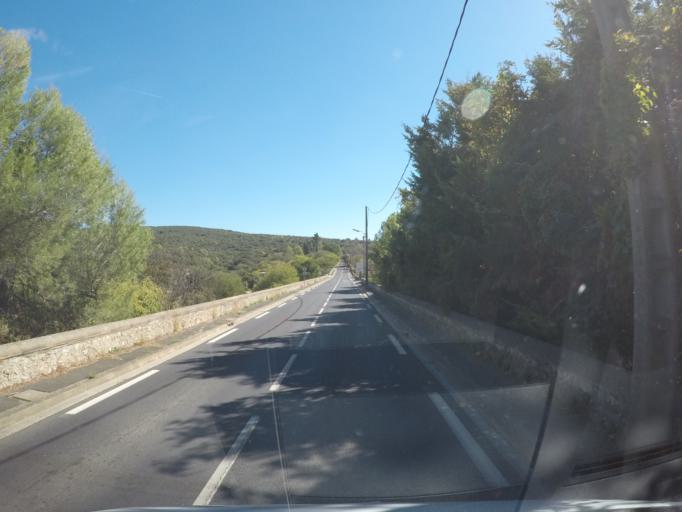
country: FR
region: Languedoc-Roussillon
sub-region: Departement de l'Herault
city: Aniane
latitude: 43.7149
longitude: 3.6184
